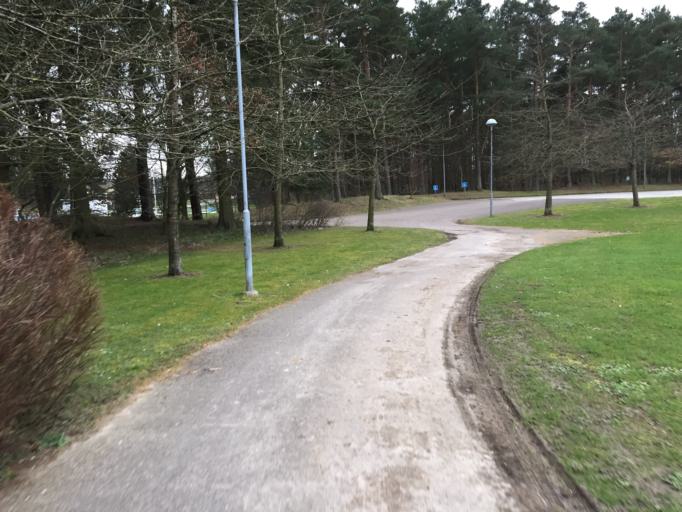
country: SE
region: Skane
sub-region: Lunds Kommun
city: Veberod
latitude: 55.6340
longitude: 13.5034
